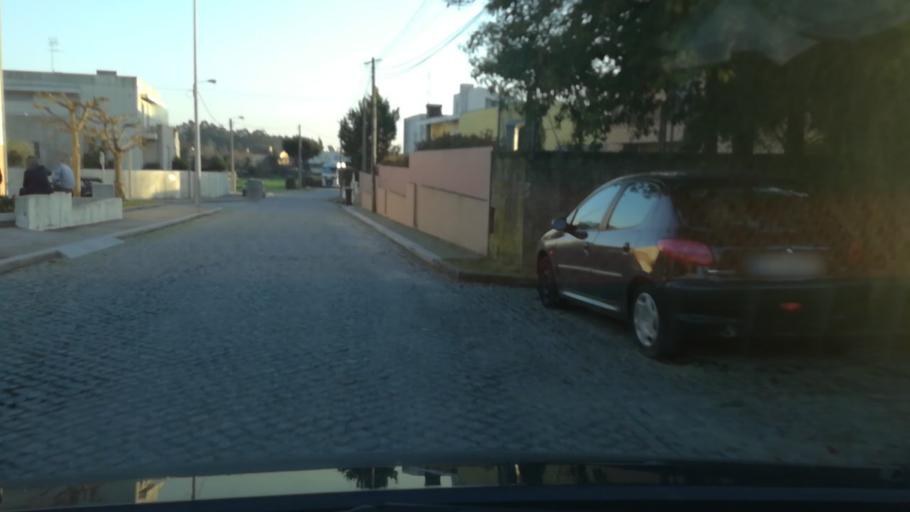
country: PT
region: Porto
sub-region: Maia
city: Anta
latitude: 41.2791
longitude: -8.6173
